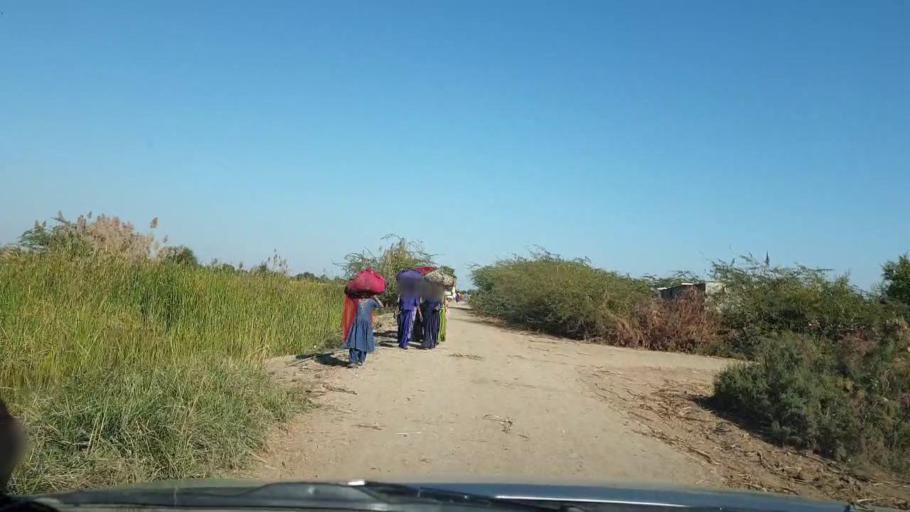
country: PK
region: Sindh
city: Berani
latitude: 25.8182
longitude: 68.9501
